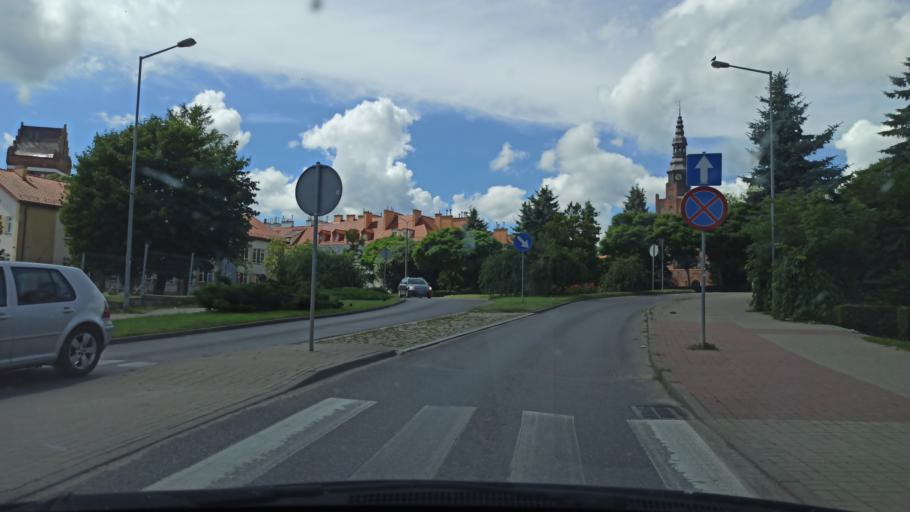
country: PL
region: Warmian-Masurian Voivodeship
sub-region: Powiat ostrodzki
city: Morag
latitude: 53.9114
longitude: 19.9299
